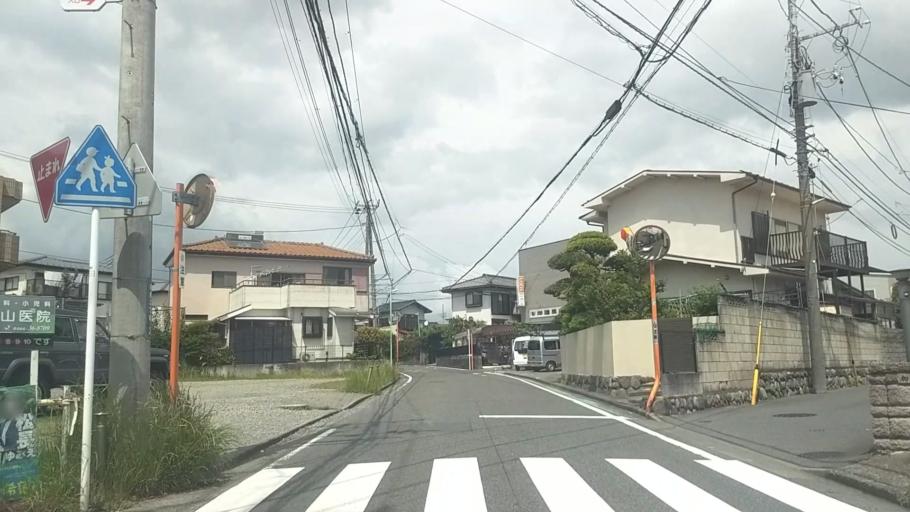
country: JP
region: Kanagawa
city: Fujisawa
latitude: 35.3429
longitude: 139.4544
